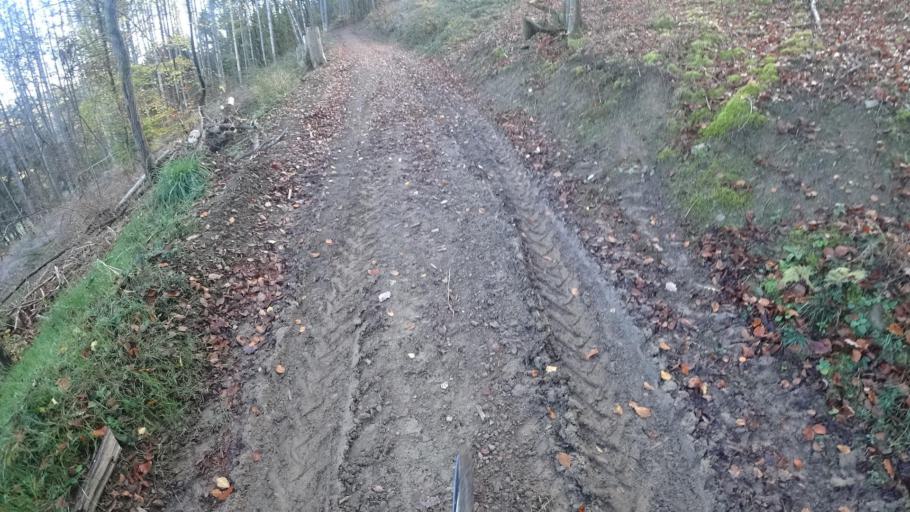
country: DE
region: Rheinland-Pfalz
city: Kirchsahr
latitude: 50.5077
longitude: 6.9130
